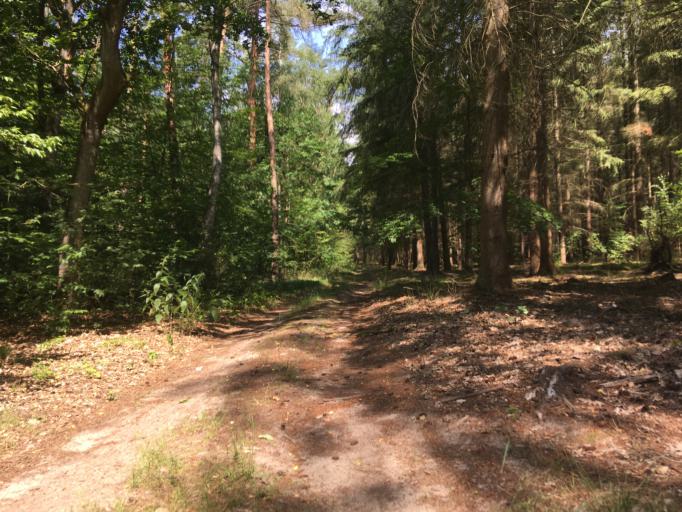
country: DE
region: Brandenburg
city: Casekow
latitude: 53.2337
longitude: 14.1201
